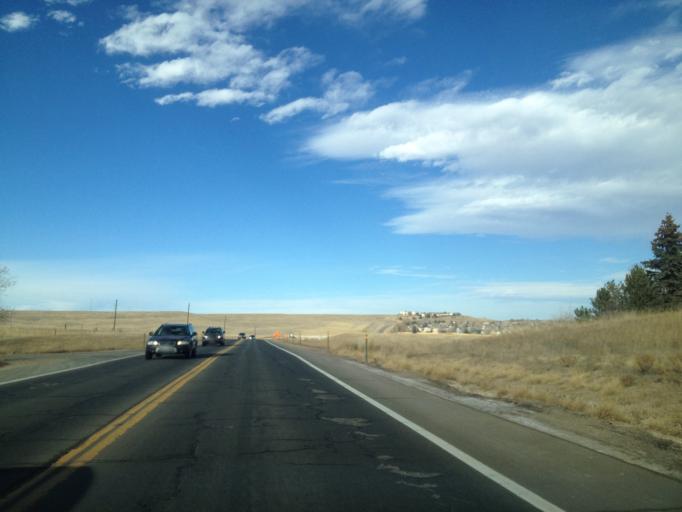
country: US
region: Colorado
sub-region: Boulder County
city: Superior
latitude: 39.9220
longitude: -105.1650
